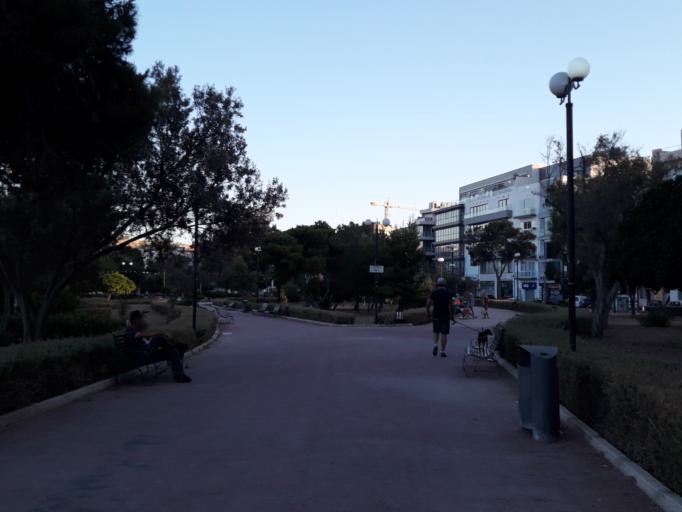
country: MT
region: Ta' Xbiex
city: Ta' Xbiex
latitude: 35.9031
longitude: 14.4951
